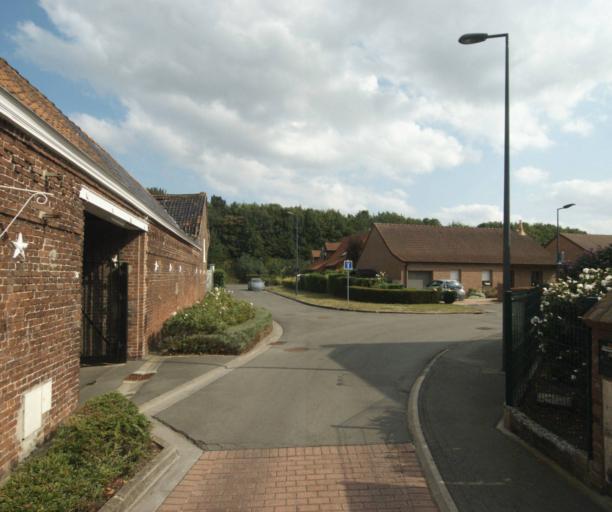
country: FR
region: Nord-Pas-de-Calais
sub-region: Departement du Nord
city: Lys-lez-Lannoy
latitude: 50.6652
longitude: 3.2200
